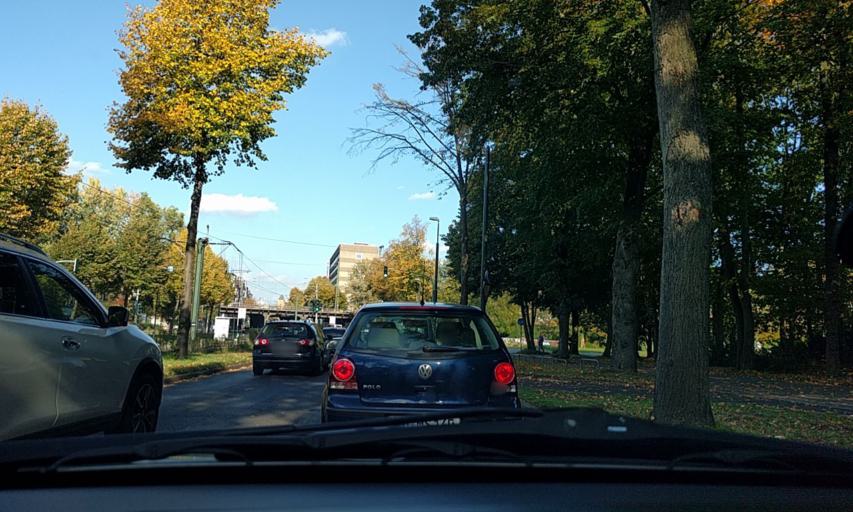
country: DE
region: North Rhine-Westphalia
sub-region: Regierungsbezirk Dusseldorf
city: Dusseldorf
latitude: 51.2081
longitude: 6.7921
